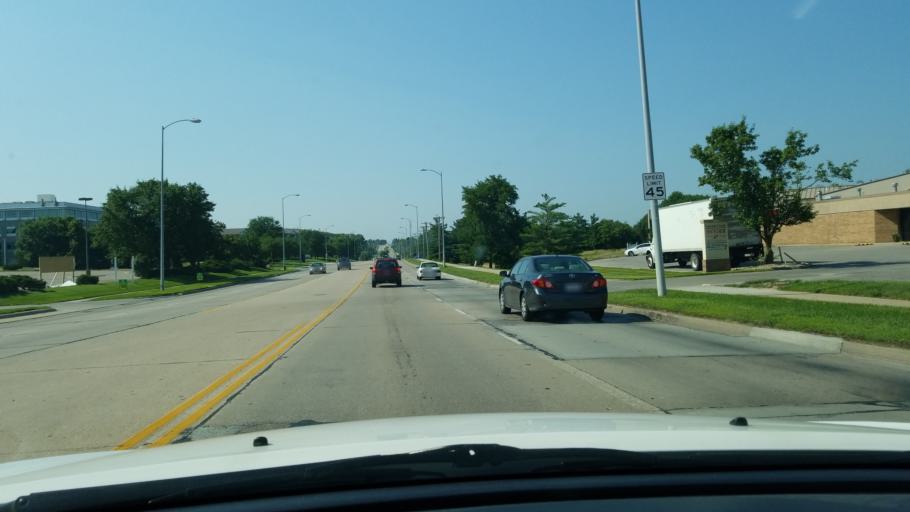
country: US
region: Nebraska
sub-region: Lancaster County
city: Lincoln
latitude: 40.7838
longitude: -96.6251
